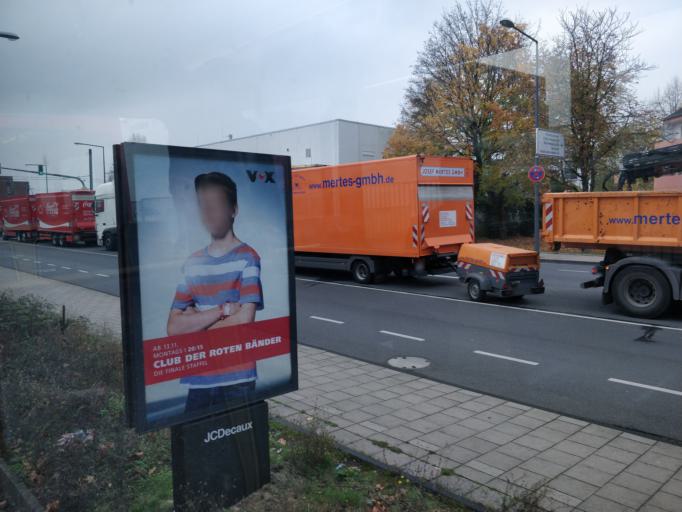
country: DE
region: North Rhine-Westphalia
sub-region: Regierungsbezirk Koln
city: Mengenich
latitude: 50.9776
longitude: 6.8985
